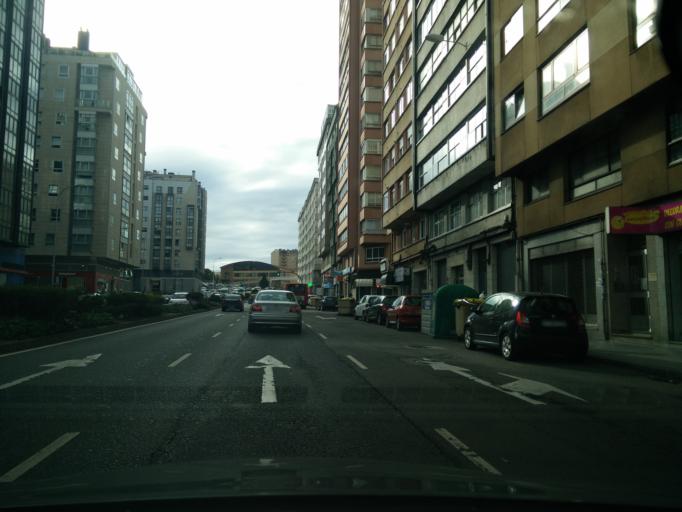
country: ES
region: Galicia
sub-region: Provincia da Coruna
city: A Coruna
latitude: 43.3561
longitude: -8.4141
